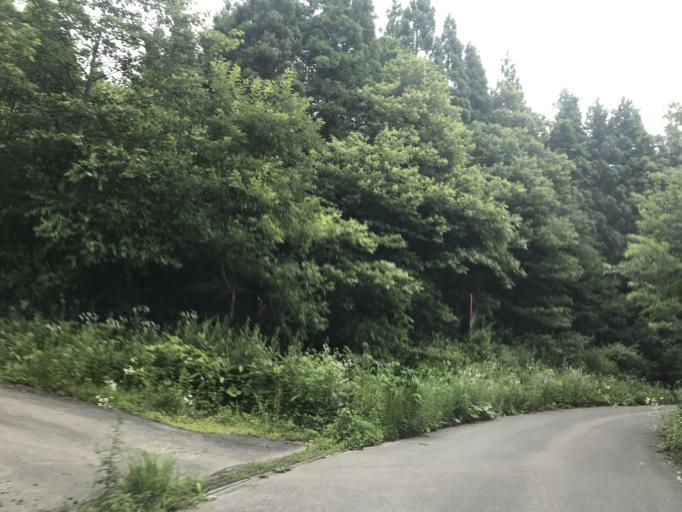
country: JP
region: Iwate
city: Ichinoseki
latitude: 38.9598
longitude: 140.8917
